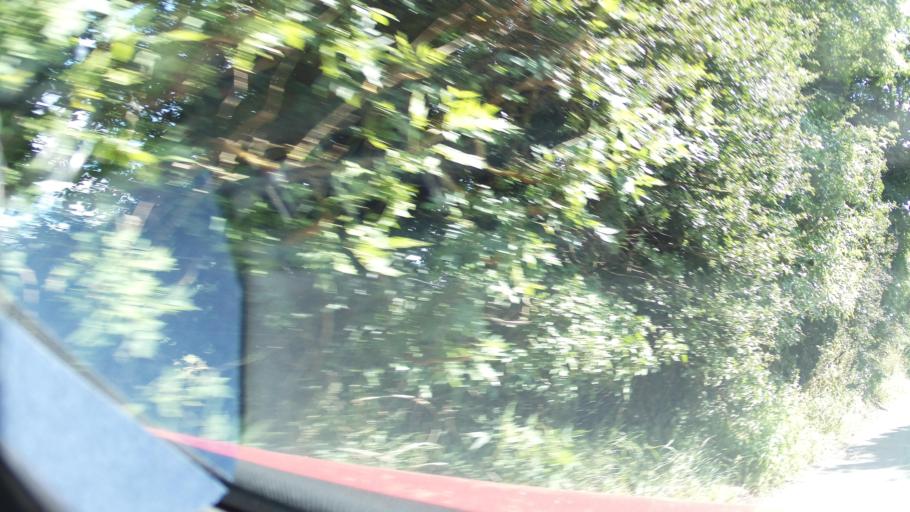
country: GB
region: England
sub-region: West Berkshire
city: Newbury
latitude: 51.4236
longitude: -1.3314
